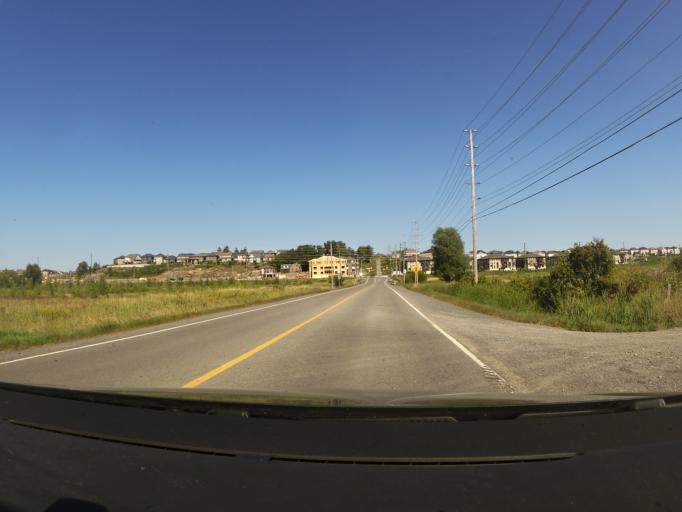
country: CA
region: Ontario
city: Bells Corners
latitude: 45.3122
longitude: -75.9418
